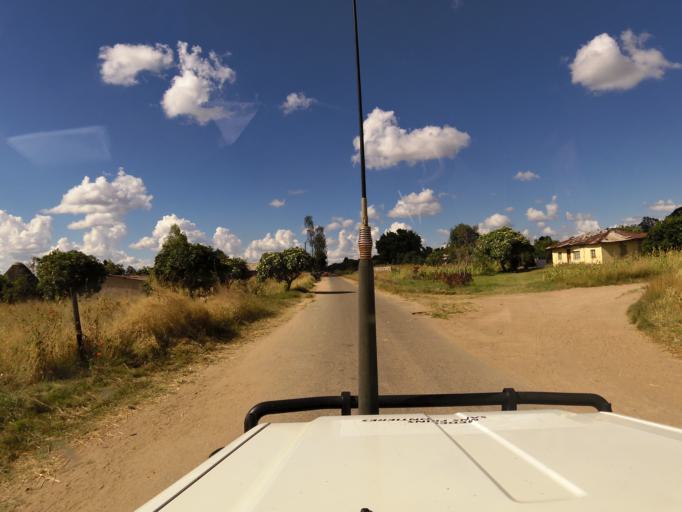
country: ZW
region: Harare
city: Epworth
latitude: -17.8742
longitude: 31.1281
